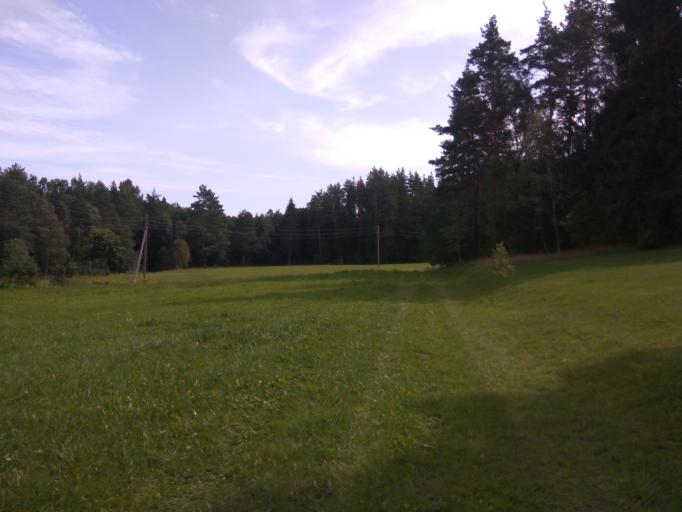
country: LV
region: Alsunga
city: Alsunga
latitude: 56.9879
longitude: 21.6731
